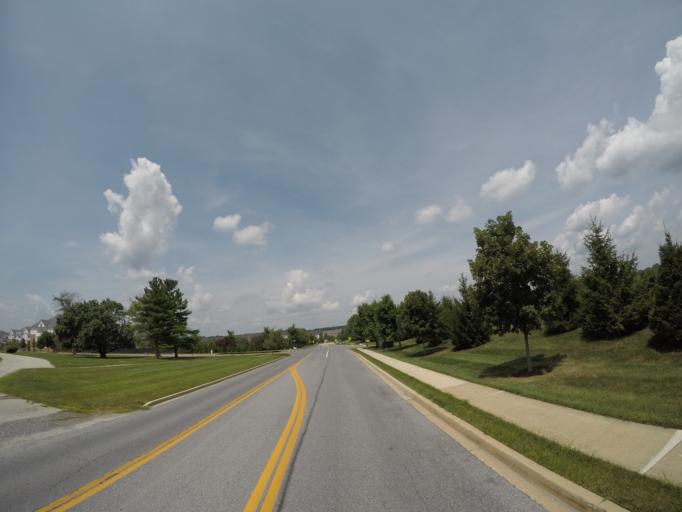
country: US
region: Maryland
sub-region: Howard County
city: North Laurel
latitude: 39.1391
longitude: -76.8508
